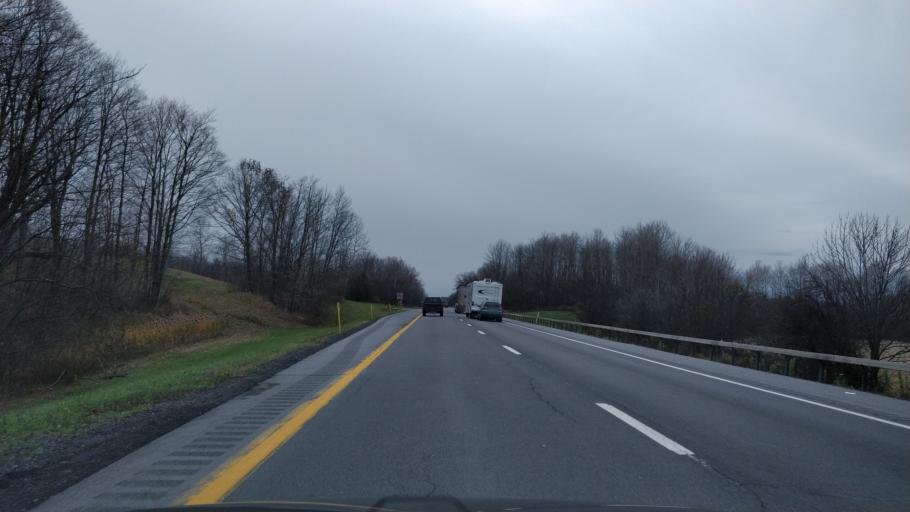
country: US
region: New York
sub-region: Jefferson County
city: Adams
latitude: 43.7732
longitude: -76.0468
